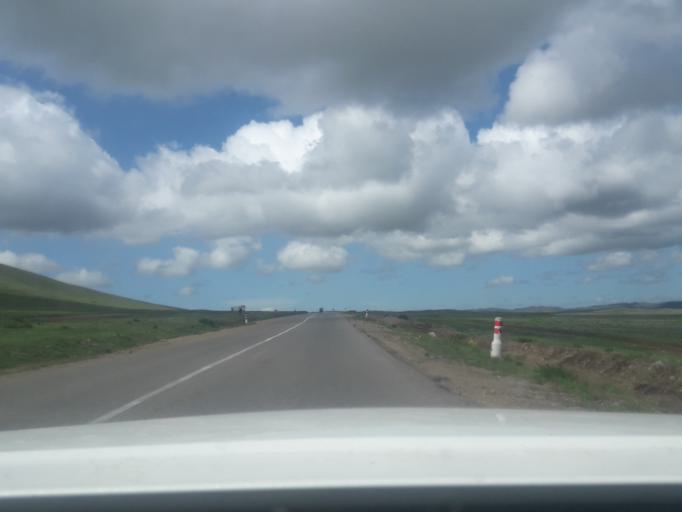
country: MN
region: Central Aimak
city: Altanbulag
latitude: 47.9003
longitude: 106.4176
